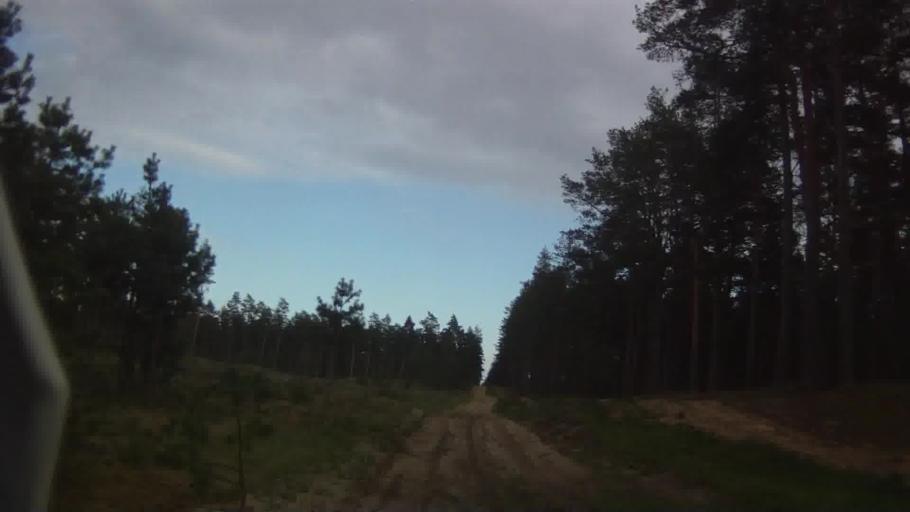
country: LV
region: Riga
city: Jaunciems
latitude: 57.0663
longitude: 24.1660
